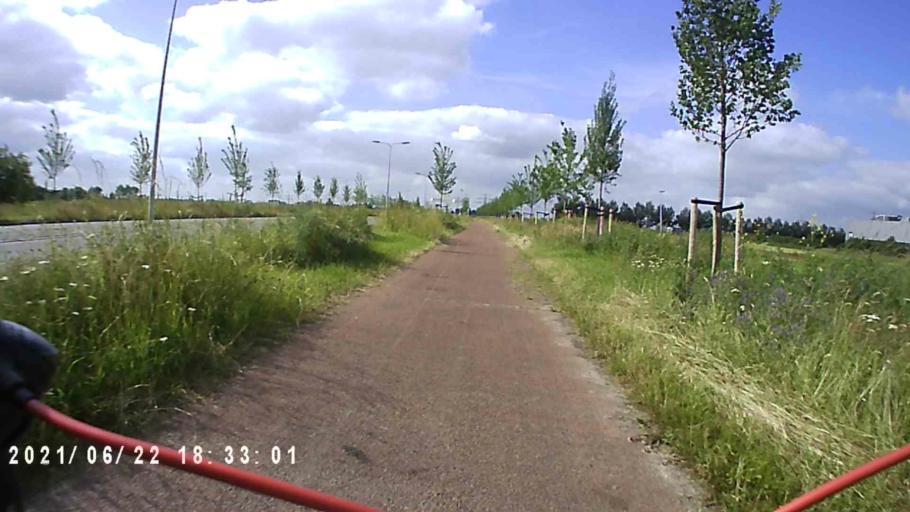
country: NL
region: Groningen
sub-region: Gemeente Zuidhorn
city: Aduard
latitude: 53.2059
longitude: 6.4723
